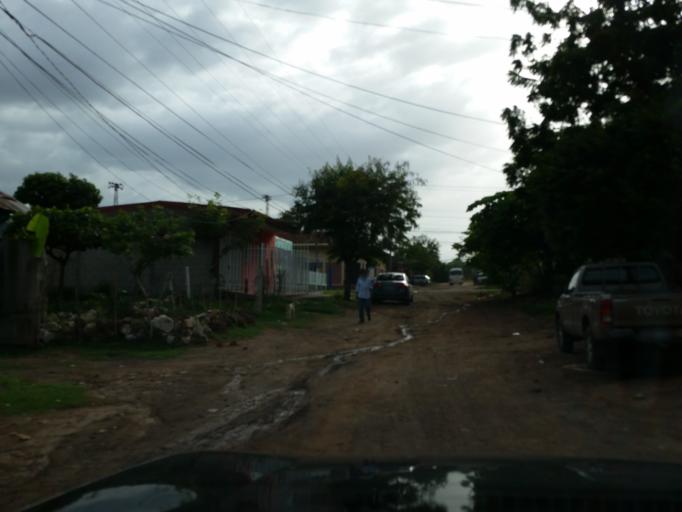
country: NI
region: Granada
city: Granada
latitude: 11.9394
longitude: -85.9615
